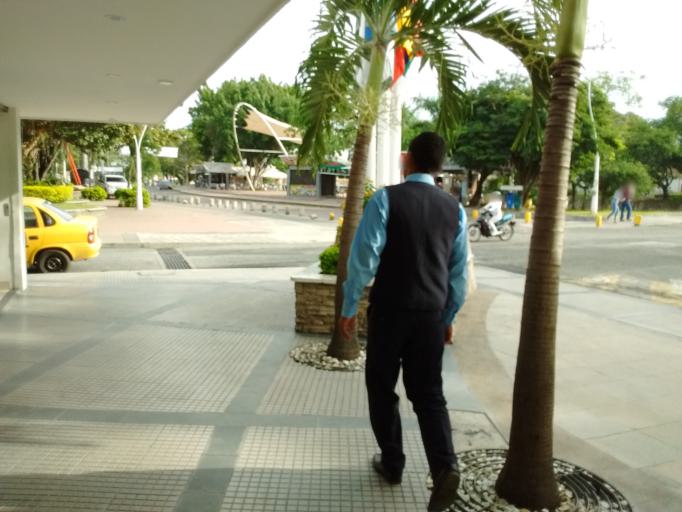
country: CO
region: Valle del Cauca
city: Tulua
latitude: 4.0835
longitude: -76.1960
